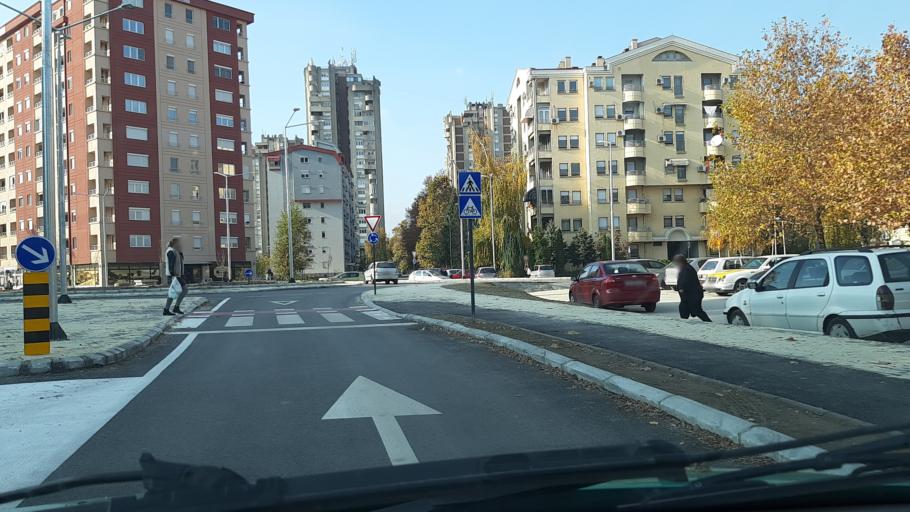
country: MK
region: Kisela Voda
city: Usje
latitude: 41.9847
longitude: 21.4567
